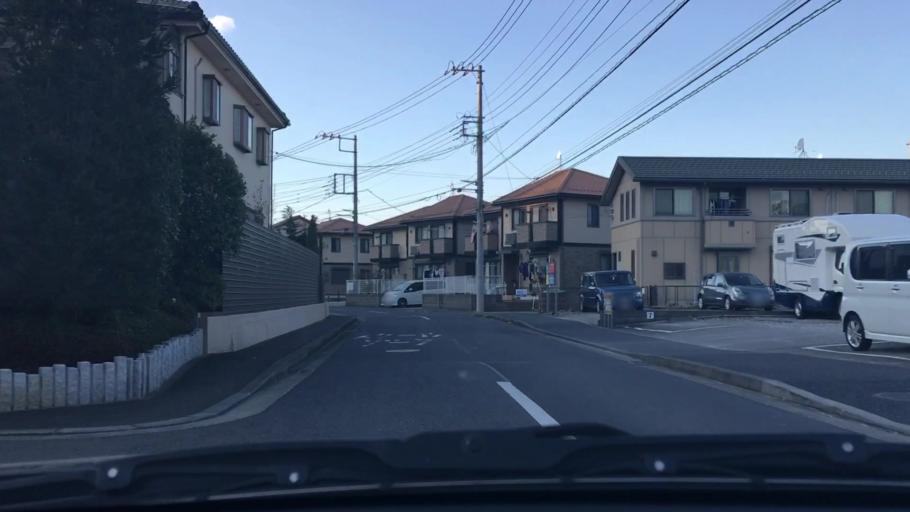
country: JP
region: Tokyo
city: Chofugaoka
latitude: 35.5498
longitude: 139.5732
